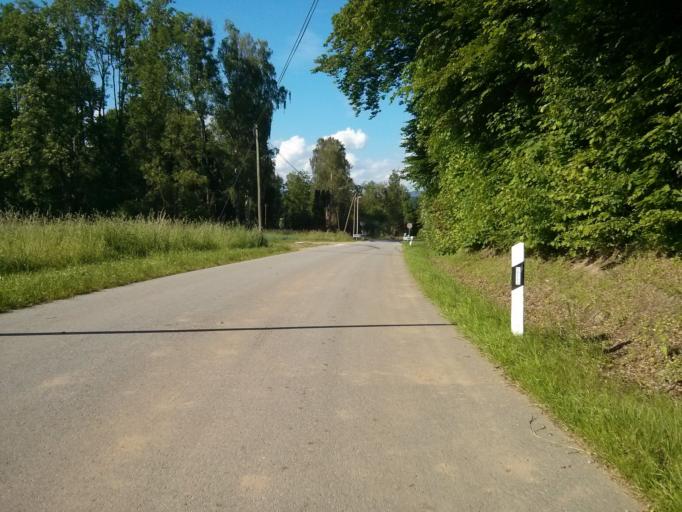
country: DE
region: Bavaria
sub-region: Lower Bavaria
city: Metten
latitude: 48.8264
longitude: 12.9092
